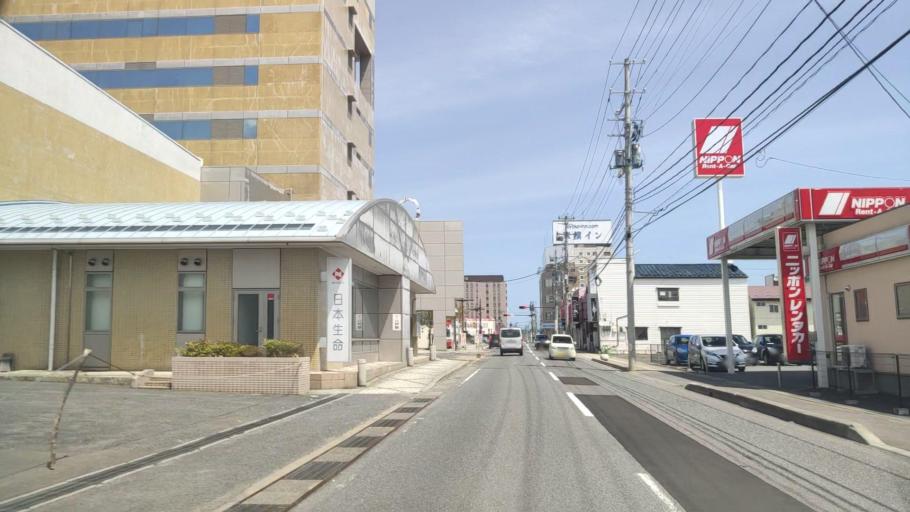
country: JP
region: Aomori
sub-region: Hachinohe Shi
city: Uchimaru
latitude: 40.5077
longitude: 141.4315
